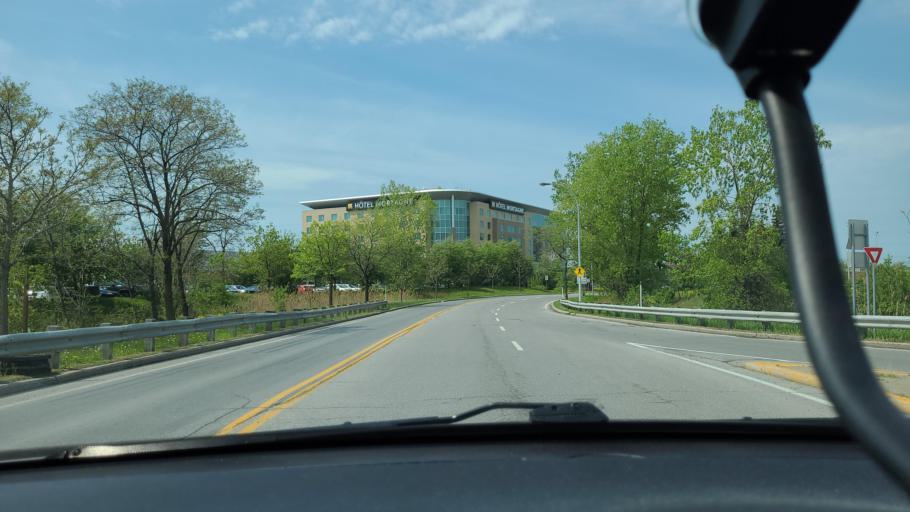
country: CA
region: Quebec
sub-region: Monteregie
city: Boucherville
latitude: 45.5700
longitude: -73.4410
